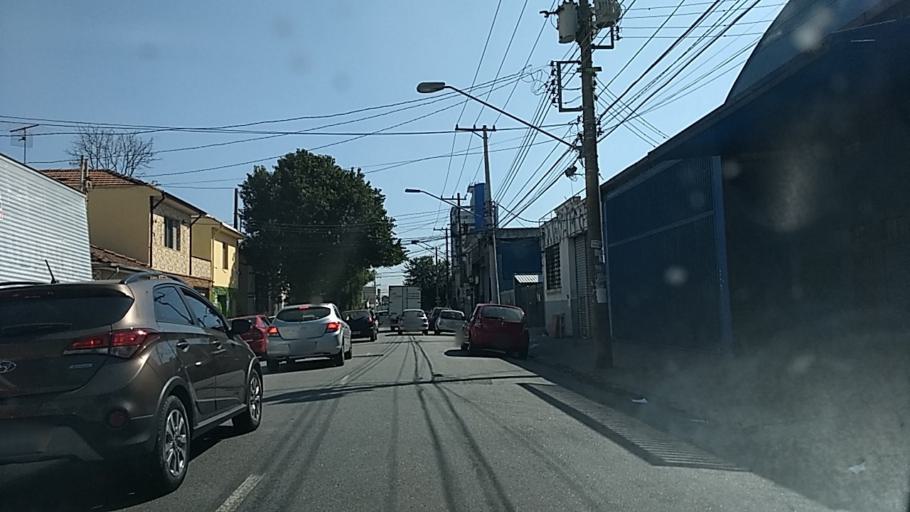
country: BR
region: Sao Paulo
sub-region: Sao Paulo
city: Sao Paulo
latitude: -23.5241
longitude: -46.5904
